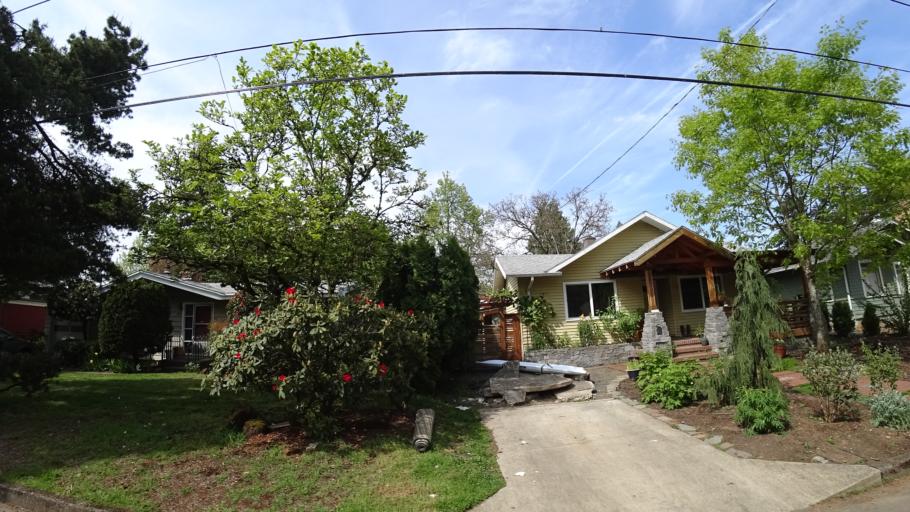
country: US
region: Oregon
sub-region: Multnomah County
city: Lents
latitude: 45.4839
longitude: -122.6030
